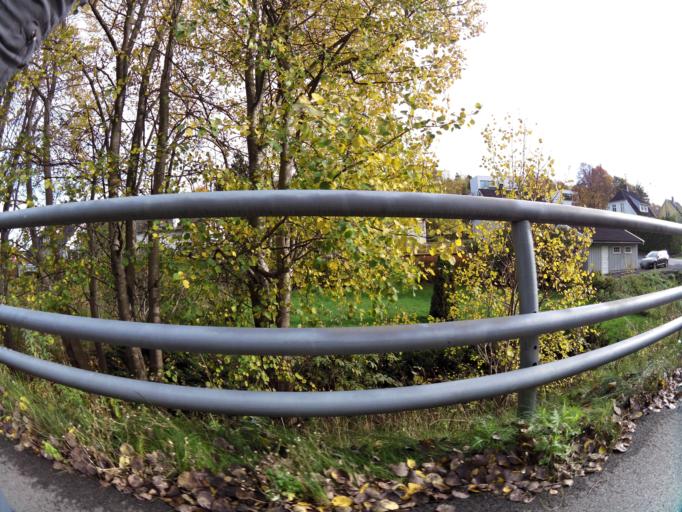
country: NO
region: Ostfold
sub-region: Fredrikstad
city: Fredrikstad
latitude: 59.2230
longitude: 10.9101
